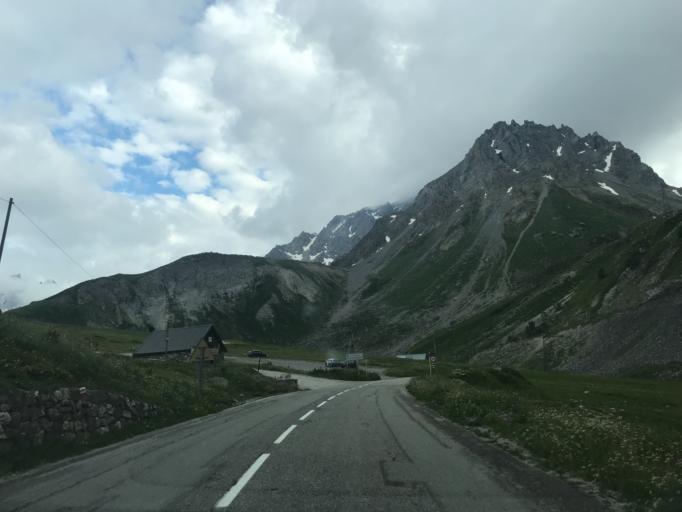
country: FR
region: Rhone-Alpes
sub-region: Departement de la Savoie
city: Valloire
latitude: 45.0909
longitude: 6.4352
